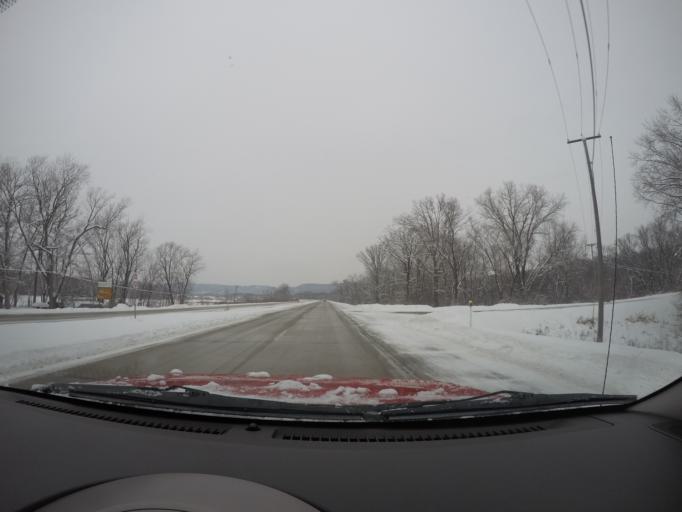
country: US
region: Minnesota
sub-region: Houston County
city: La Crescent
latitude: 43.8208
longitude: -91.2786
